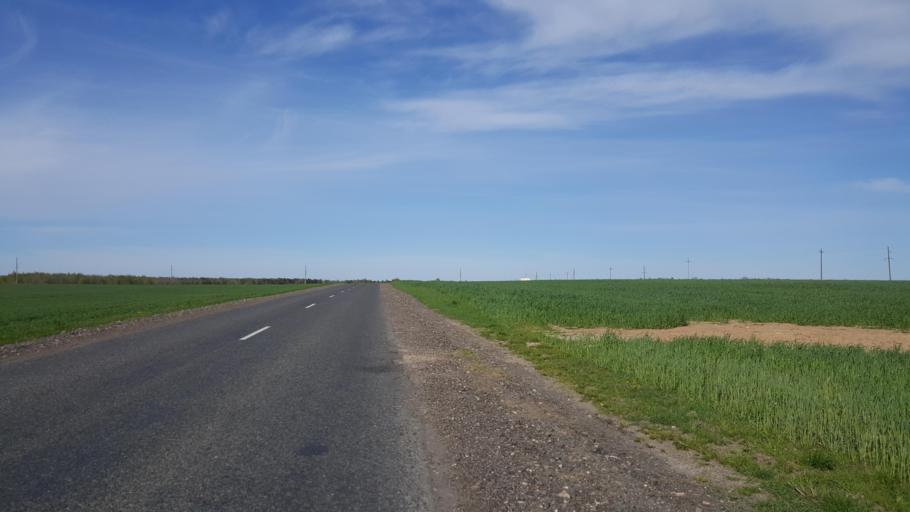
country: BY
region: Brest
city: Vysokaye
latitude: 52.3897
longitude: 23.4607
